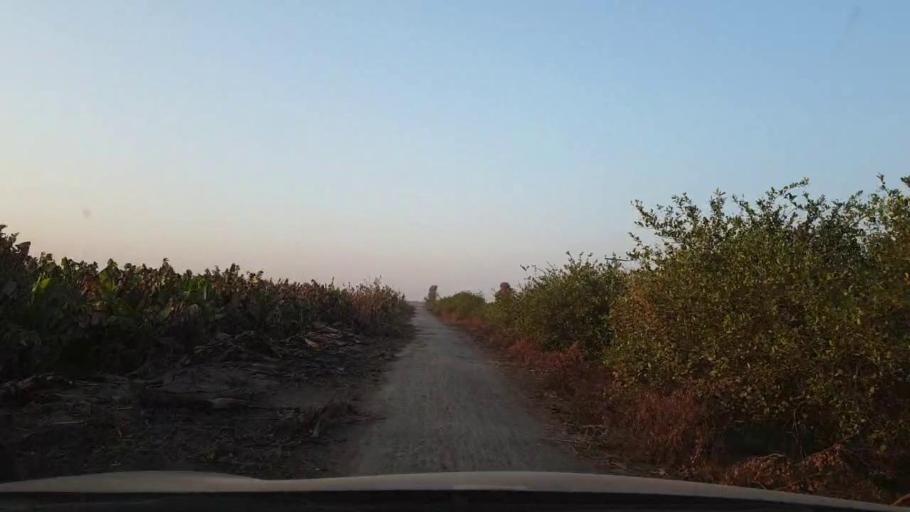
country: PK
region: Sindh
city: Tando Allahyar
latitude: 25.5182
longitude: 68.7379
